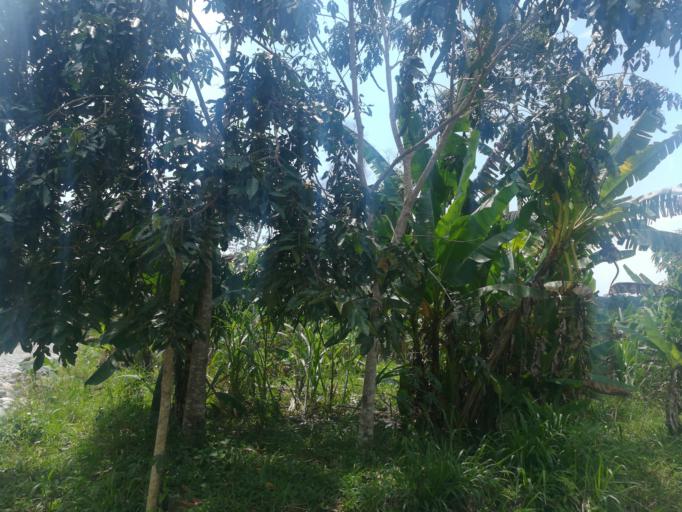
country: EC
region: Napo
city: Tena
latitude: -1.0313
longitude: -77.6781
